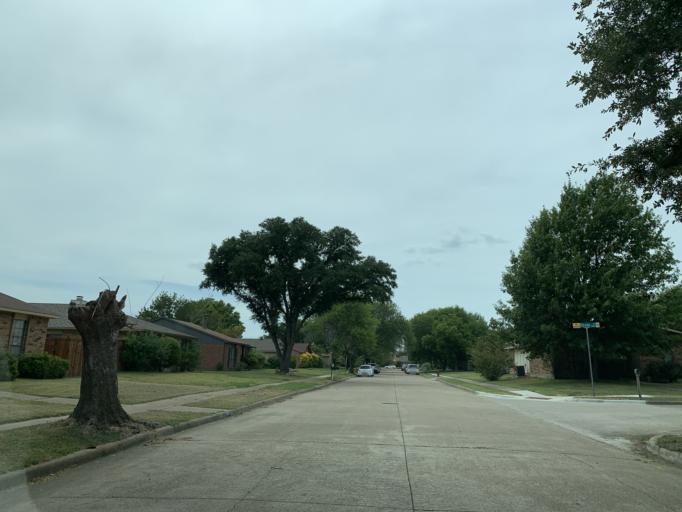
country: US
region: Texas
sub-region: Dallas County
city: Cedar Hill
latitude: 32.6524
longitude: -97.0321
